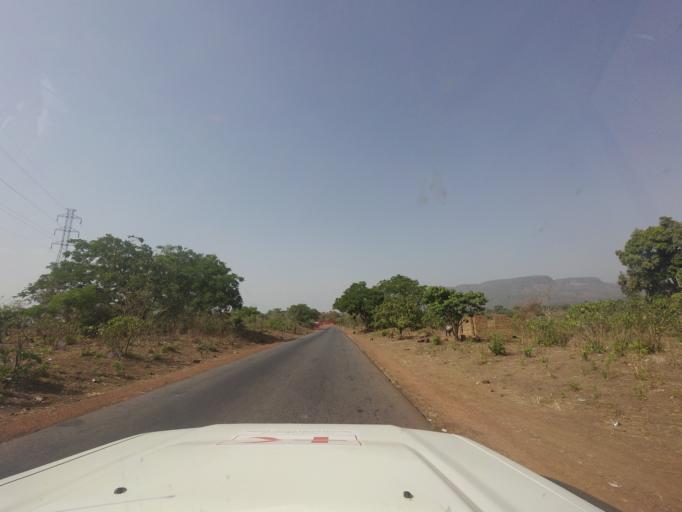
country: GN
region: Mamou
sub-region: Mamou Prefecture
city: Mamou
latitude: 10.2527
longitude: -12.4581
